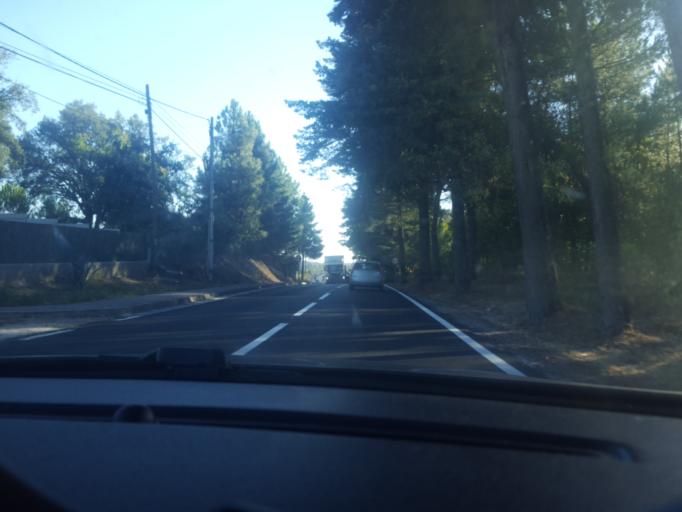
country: PT
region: Viseu
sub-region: Mangualde
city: Mangualde
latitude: 40.5799
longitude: -7.8072
